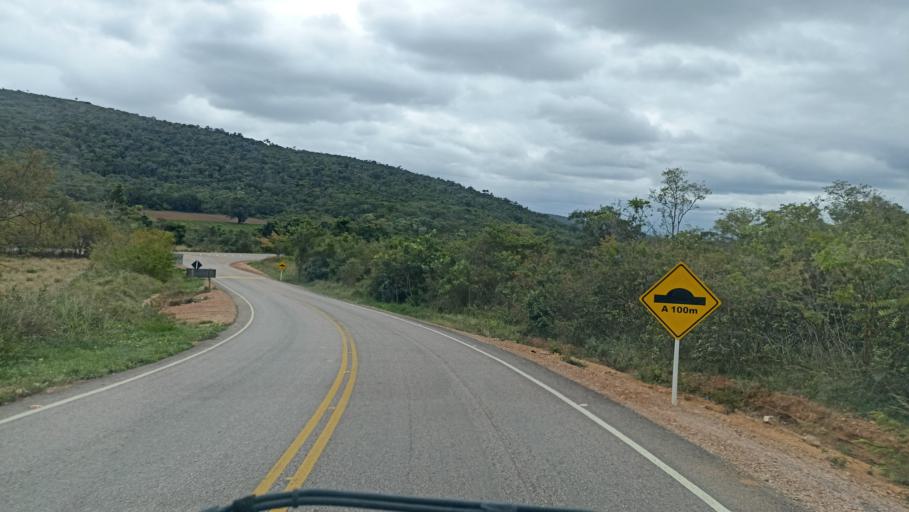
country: BR
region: Bahia
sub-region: Andarai
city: Vera Cruz
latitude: -12.9248
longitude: -41.2320
